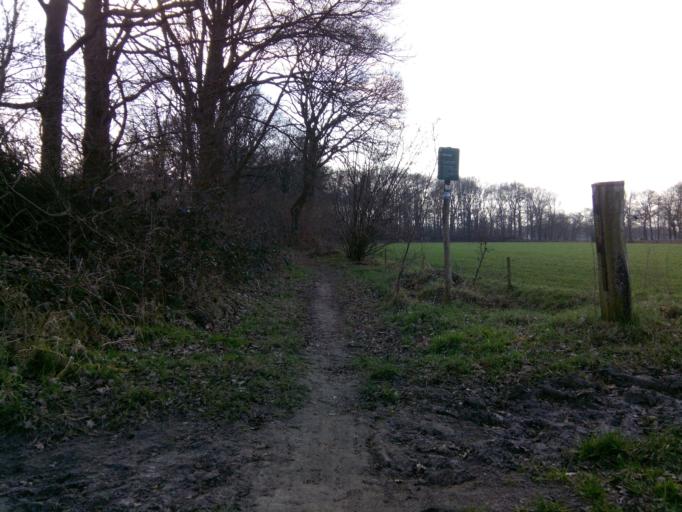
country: NL
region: Utrecht
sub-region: Gemeente Woudenberg
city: Woudenberg
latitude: 52.0947
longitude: 5.4599
